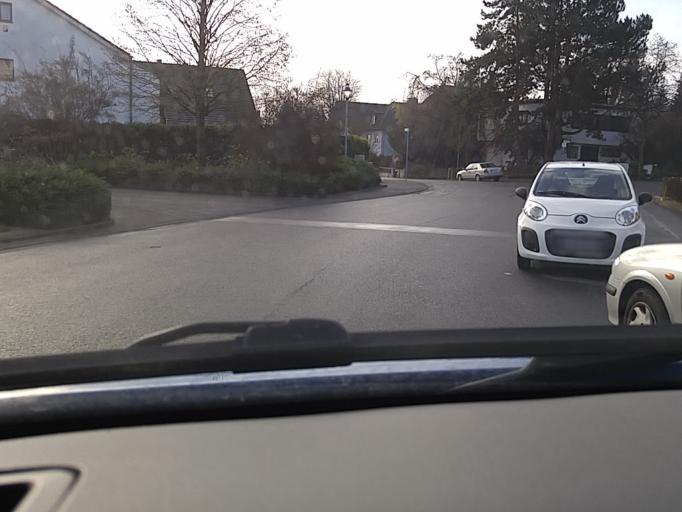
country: DE
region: Hesse
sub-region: Regierungsbezirk Darmstadt
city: Bad Nauheim
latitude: 50.3617
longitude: 8.7326
